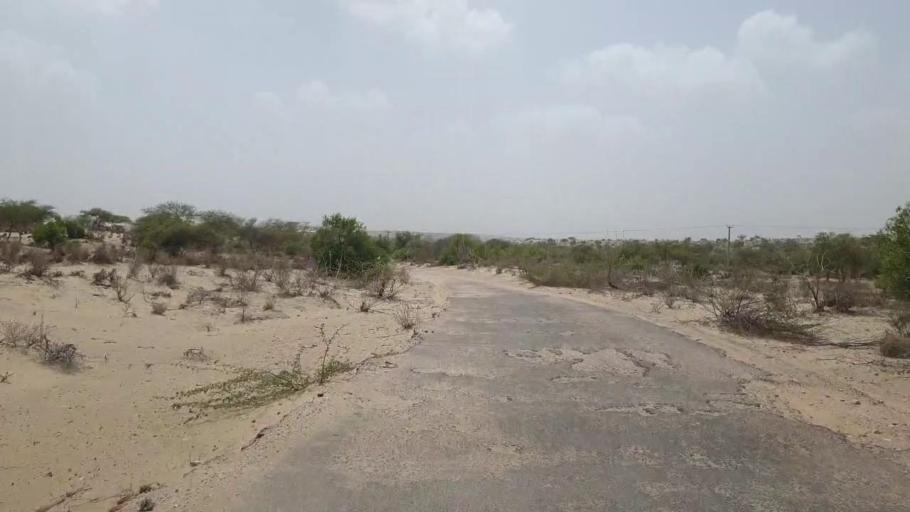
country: PK
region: Sindh
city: Diplo
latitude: 24.3914
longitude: 69.4499
